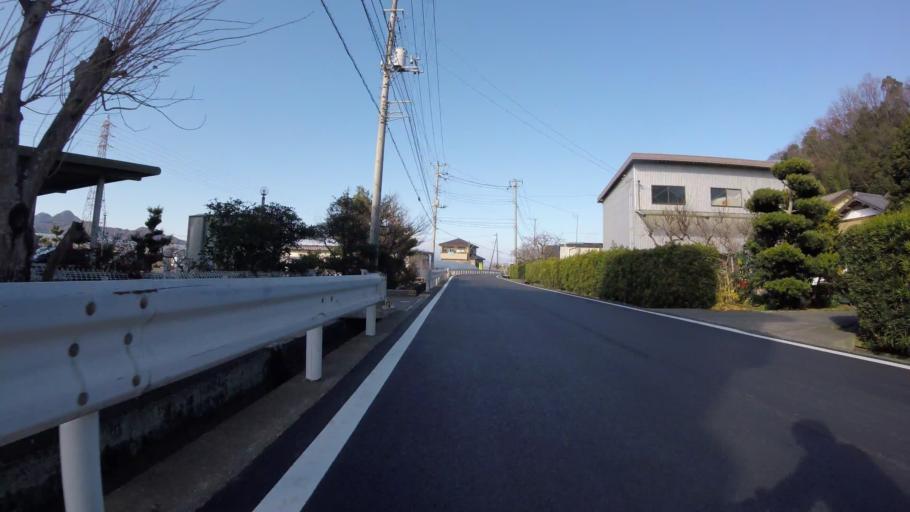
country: JP
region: Shizuoka
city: Mishima
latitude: 35.0490
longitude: 138.9527
